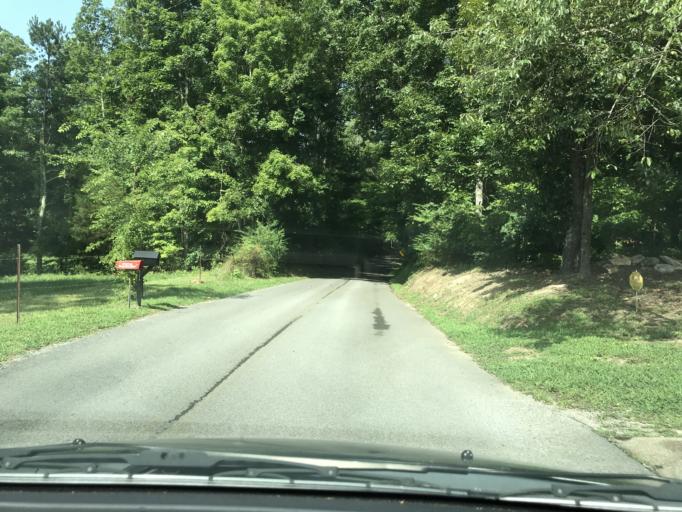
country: US
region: Tennessee
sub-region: Hamilton County
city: Collegedale
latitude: 35.0864
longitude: -84.9845
